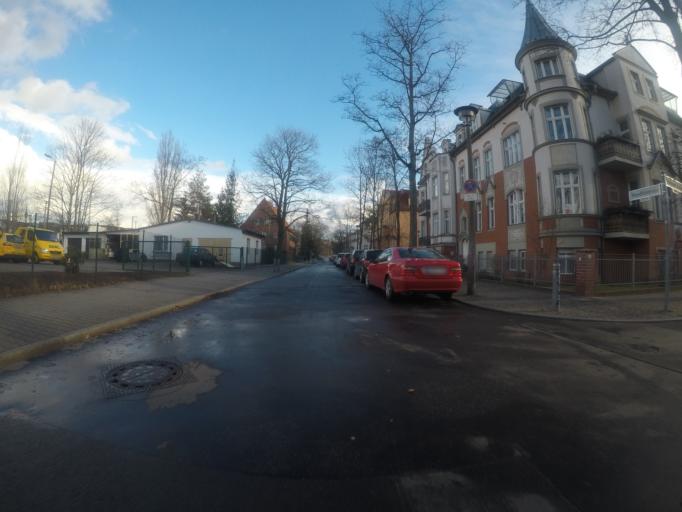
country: DE
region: Berlin
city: Karlshorst
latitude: 52.4815
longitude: 13.5221
